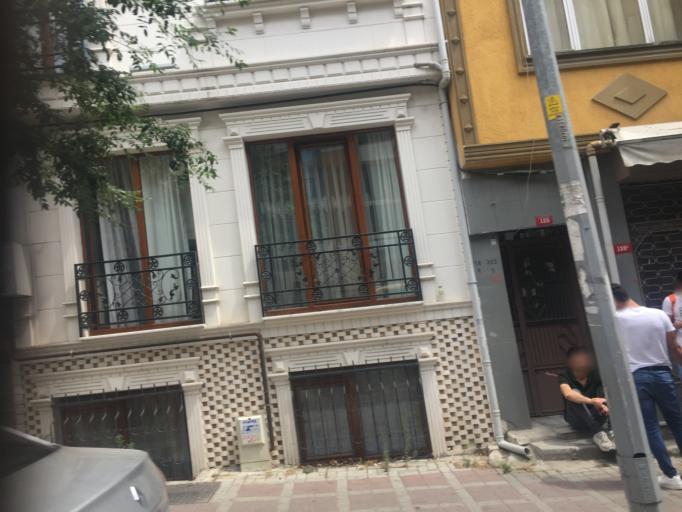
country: TR
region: Istanbul
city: Esenler
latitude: 41.0543
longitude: 28.9007
